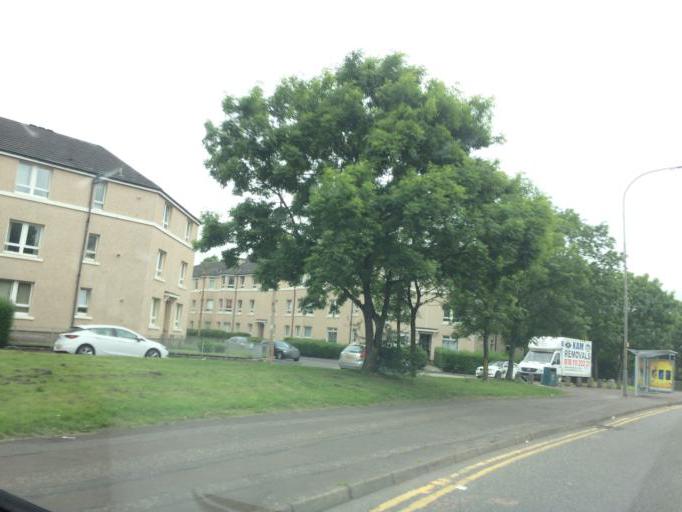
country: GB
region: Scotland
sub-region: East Renfrewshire
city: Giffnock
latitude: 55.8490
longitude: -4.3196
